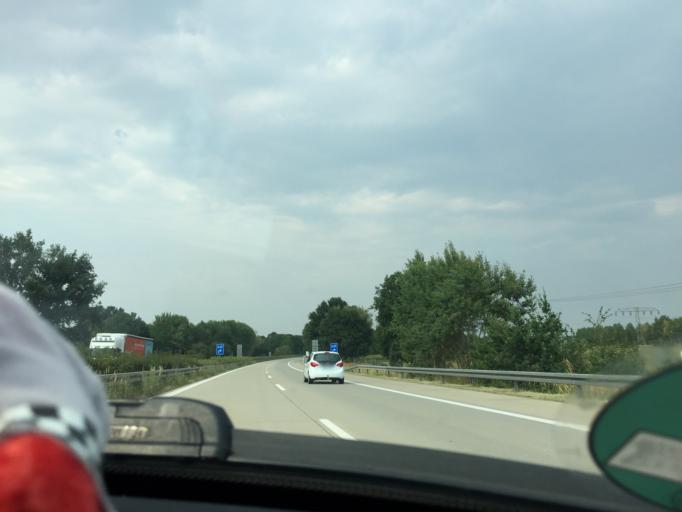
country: DE
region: Brandenburg
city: Schipkau
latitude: 51.5250
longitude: 13.9052
